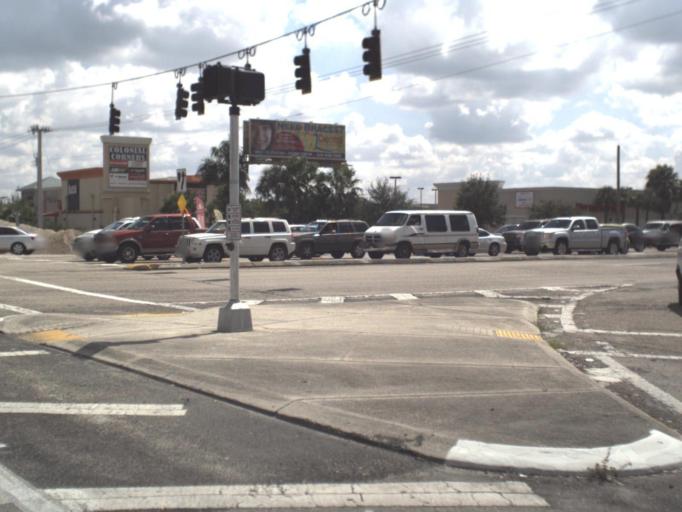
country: US
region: Florida
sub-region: Lee County
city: Fort Myers
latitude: 26.6126
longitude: -81.8116
